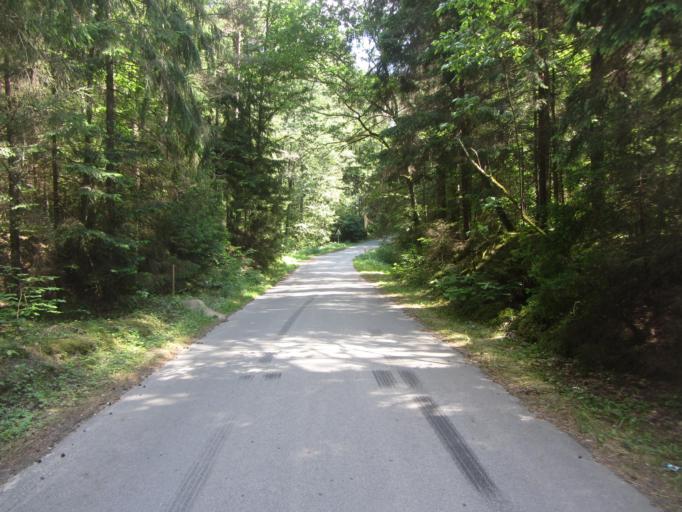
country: LT
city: Birstonas
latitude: 54.5491
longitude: 24.0102
